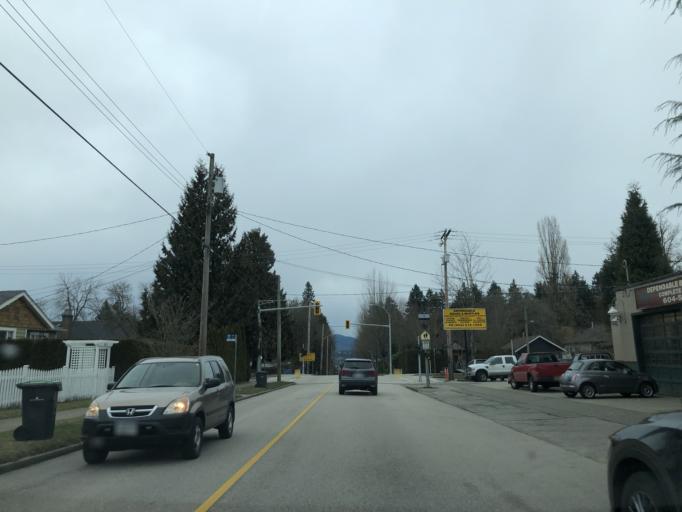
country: CA
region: British Columbia
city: New Westminster
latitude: 49.2160
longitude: -122.9149
